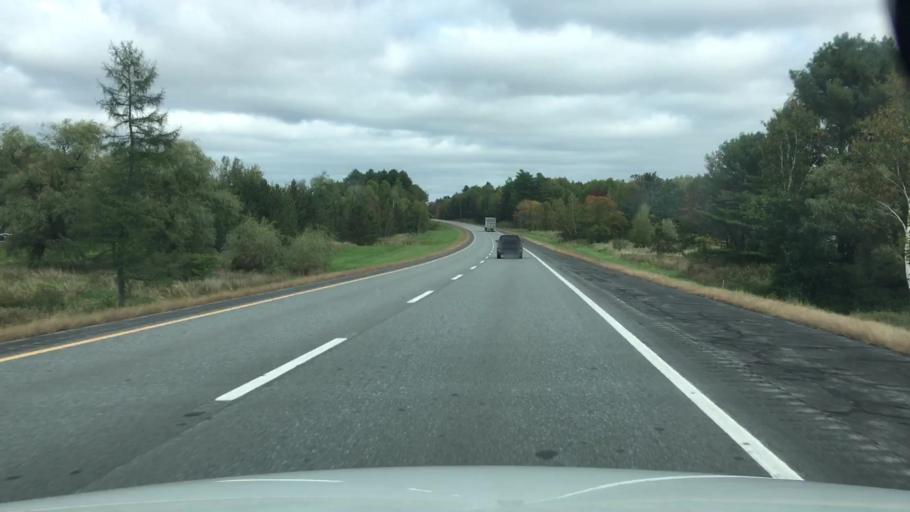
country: US
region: Maine
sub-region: Somerset County
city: Pittsfield
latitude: 44.8057
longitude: -69.3694
